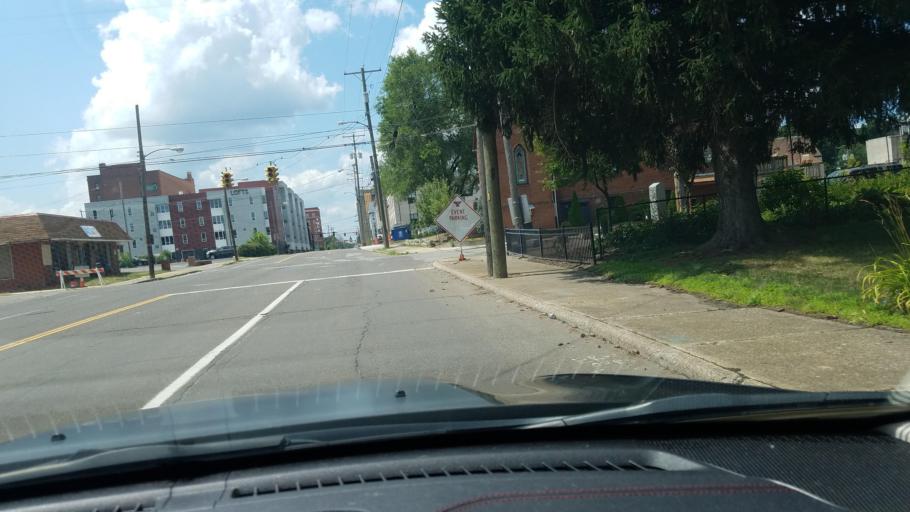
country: US
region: Ohio
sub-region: Mahoning County
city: Youngstown
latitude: 41.1018
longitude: -80.6444
